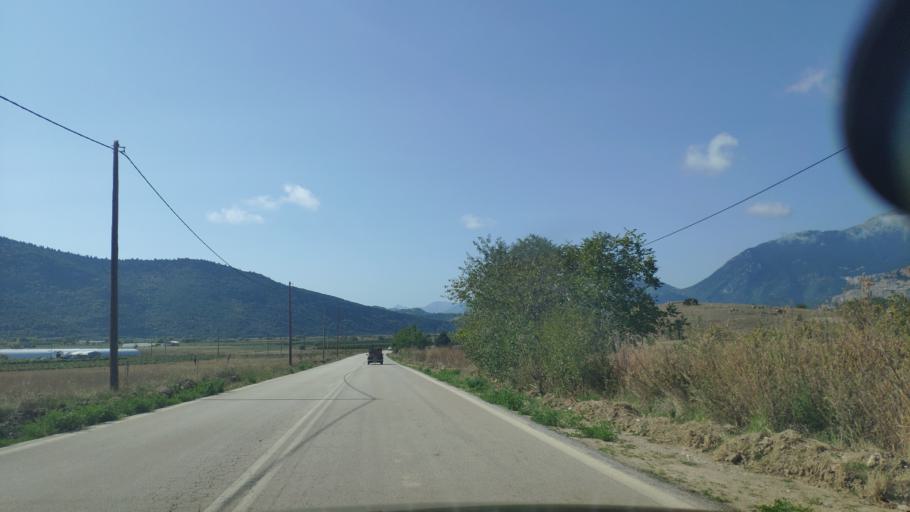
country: GR
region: Peloponnese
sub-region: Nomos Korinthias
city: Xylokastro
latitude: 37.9480
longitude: 22.5717
